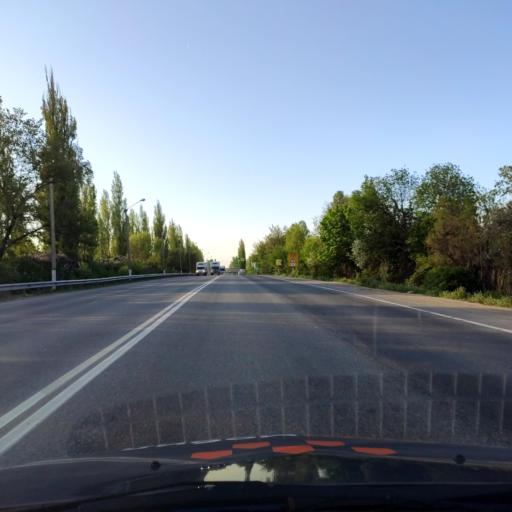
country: RU
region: Lipetsk
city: Yelets
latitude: 52.6035
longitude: 38.4695
